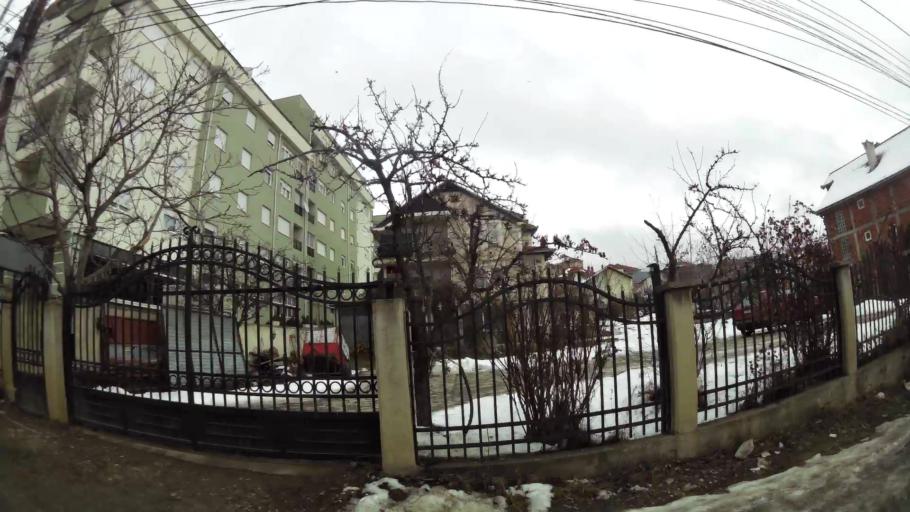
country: XK
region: Pristina
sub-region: Komuna e Prishtines
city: Pristina
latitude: 42.6528
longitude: 21.1921
